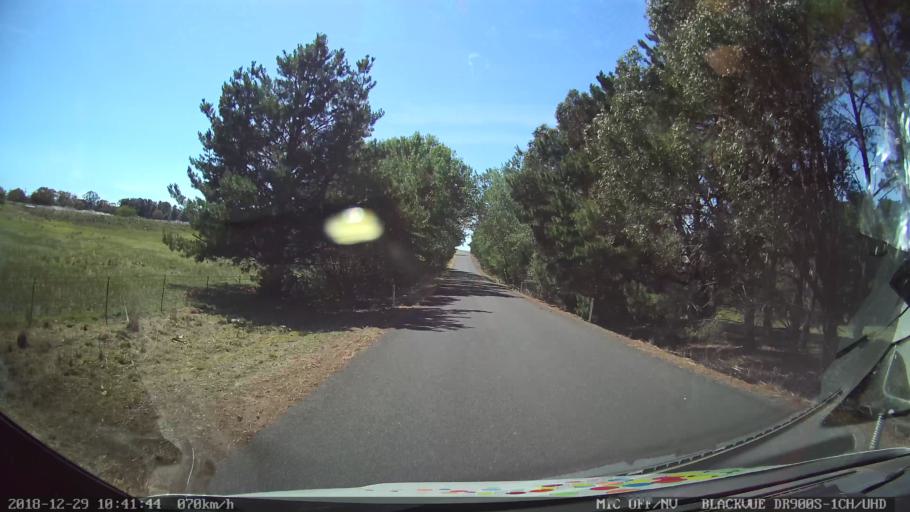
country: AU
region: New South Wales
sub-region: Palerang
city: Bungendore
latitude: -35.0281
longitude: 149.5227
